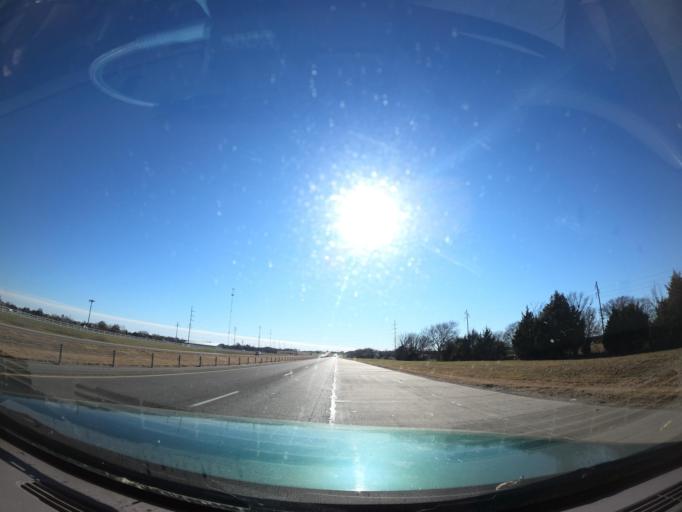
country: US
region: Oklahoma
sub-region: McIntosh County
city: Checotah
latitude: 35.4697
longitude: -95.5390
